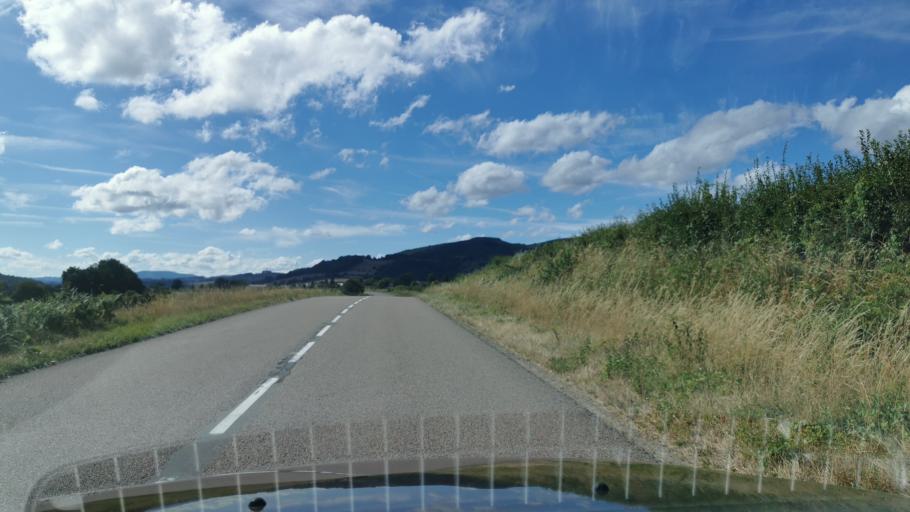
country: FR
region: Bourgogne
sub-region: Departement de Saone-et-Loire
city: Marmagne
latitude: 46.8585
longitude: 4.3104
